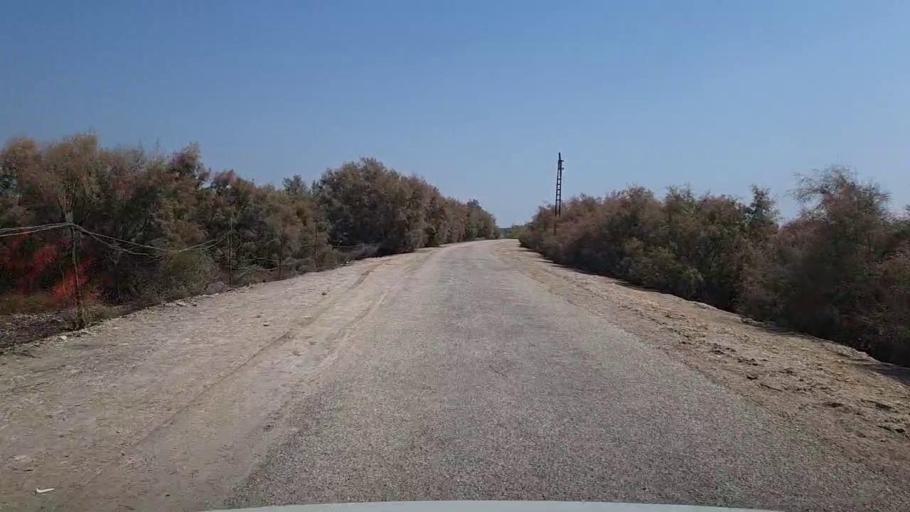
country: PK
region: Sindh
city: Kandhkot
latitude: 28.3005
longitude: 69.3515
